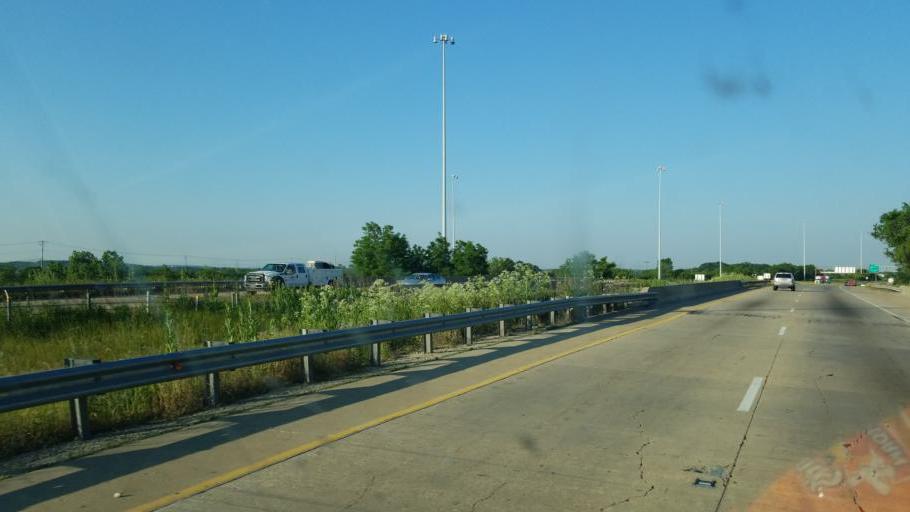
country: US
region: Illinois
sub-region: Will County
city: Shorewood
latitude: 41.4924
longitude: -88.1671
